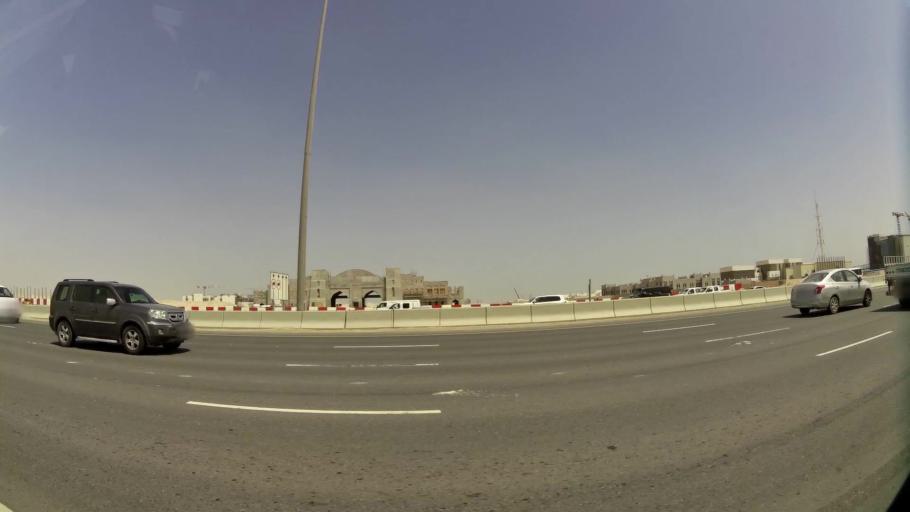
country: QA
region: Baladiyat ar Rayyan
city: Ar Rayyan
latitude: 25.3558
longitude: 51.4521
